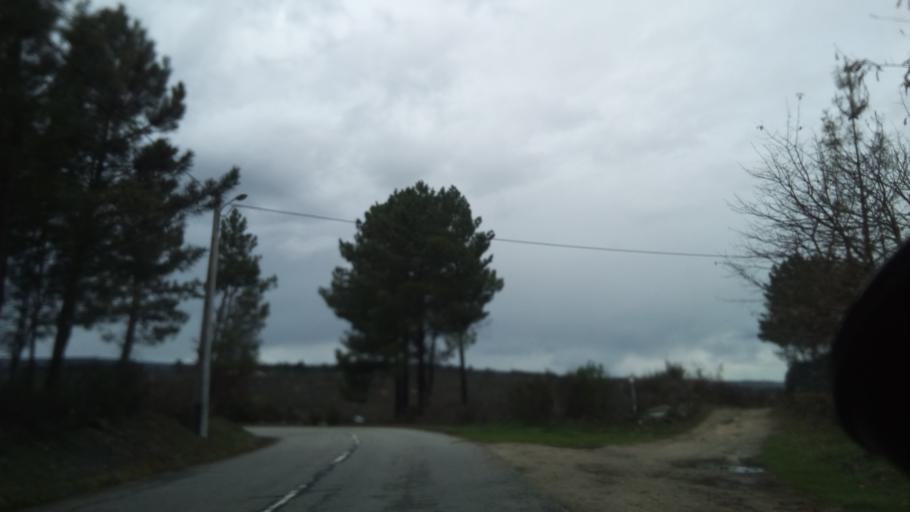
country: PT
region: Guarda
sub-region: Fornos de Algodres
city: Fornos de Algodres
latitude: 40.5934
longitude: -7.4939
